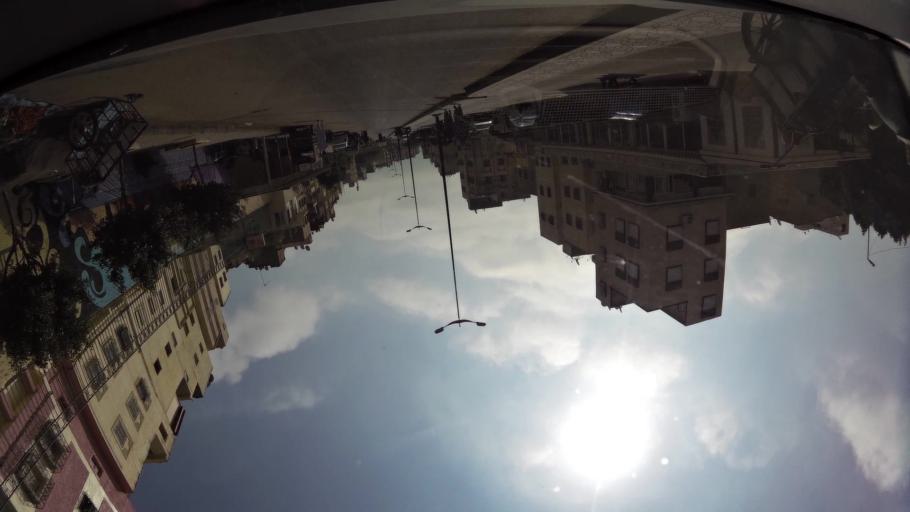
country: MA
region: Fes-Boulemane
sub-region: Fes
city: Fes
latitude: 34.0673
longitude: -5.0107
